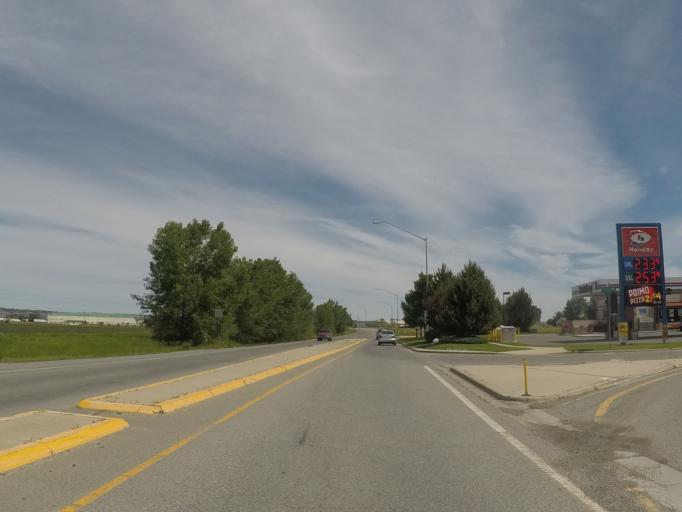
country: US
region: Montana
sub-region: Yellowstone County
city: Billings
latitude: 45.7365
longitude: -108.6091
